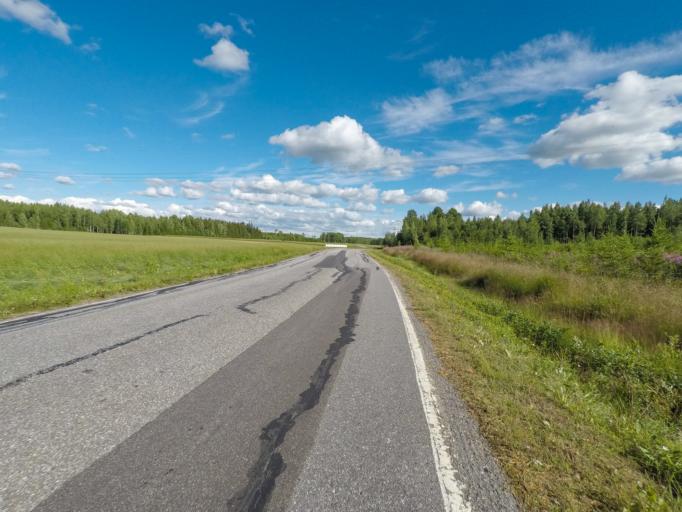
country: FI
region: South Karelia
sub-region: Imatra
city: Imatra
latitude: 61.1386
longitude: 28.6482
